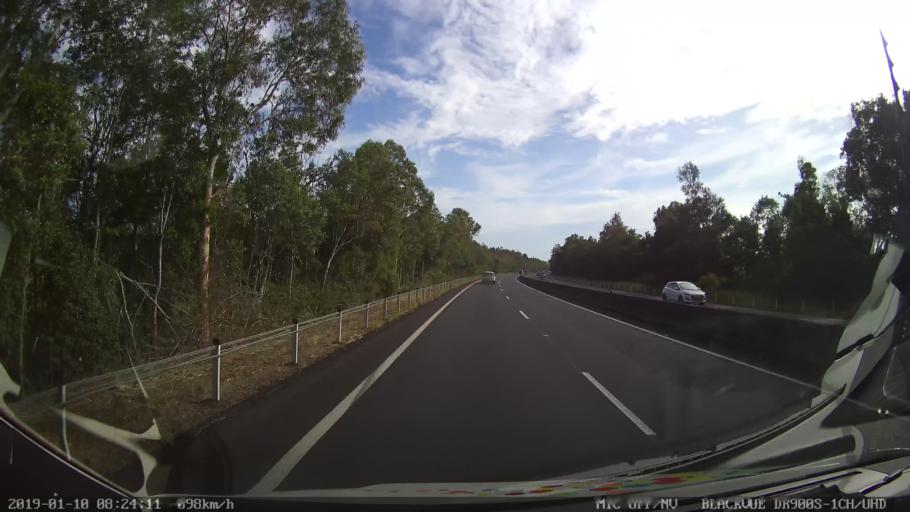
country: AU
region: New South Wales
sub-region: Coffs Harbour
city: Bonville
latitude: -30.4488
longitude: 153.0048
